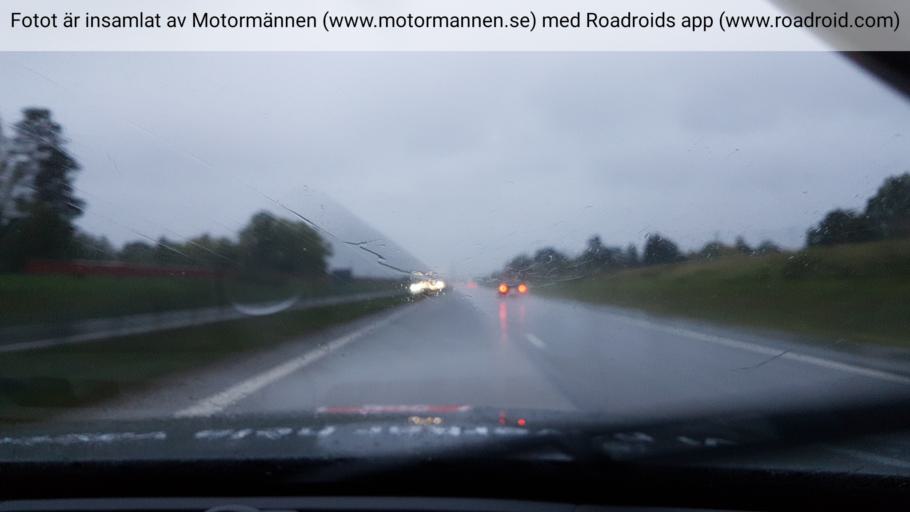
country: SE
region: Uppsala
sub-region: Uppsala Kommun
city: Gamla Uppsala
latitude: 59.9238
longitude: 17.6562
